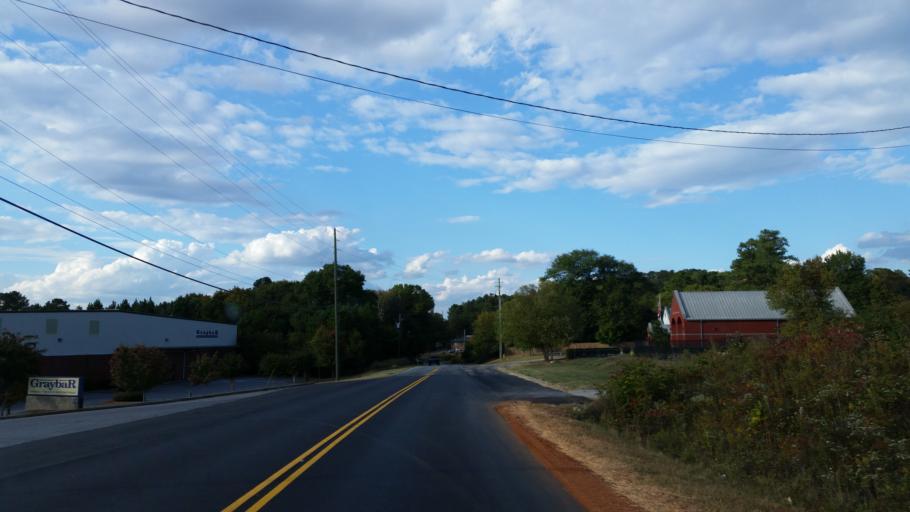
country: US
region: Georgia
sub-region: Bartow County
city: Cartersville
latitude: 34.2097
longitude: -84.8006
